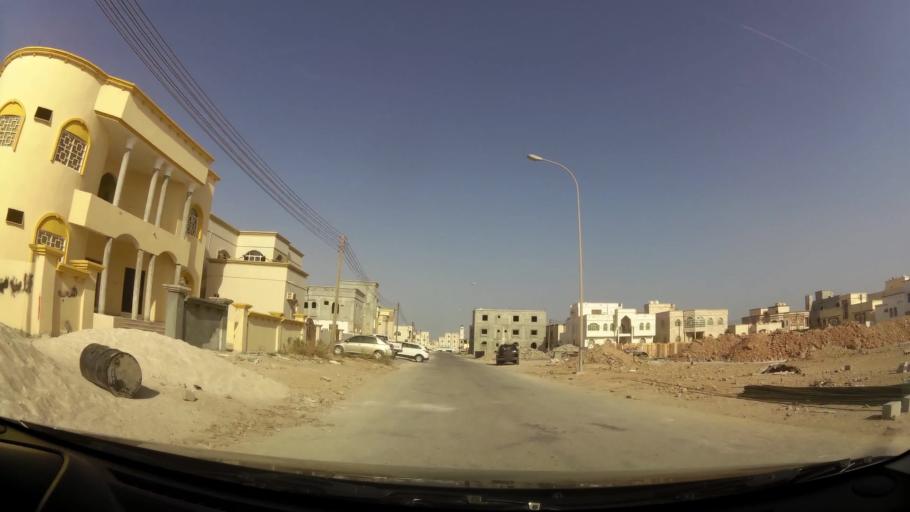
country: OM
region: Zufar
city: Salalah
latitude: 17.0166
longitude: 54.0150
